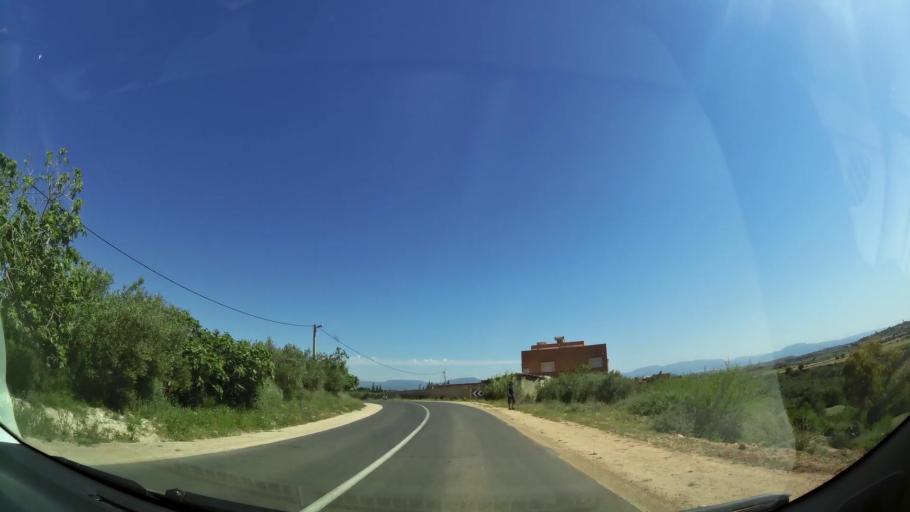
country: MA
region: Oriental
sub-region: Berkane-Taourirt
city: Madagh
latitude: 35.0403
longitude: -2.4258
